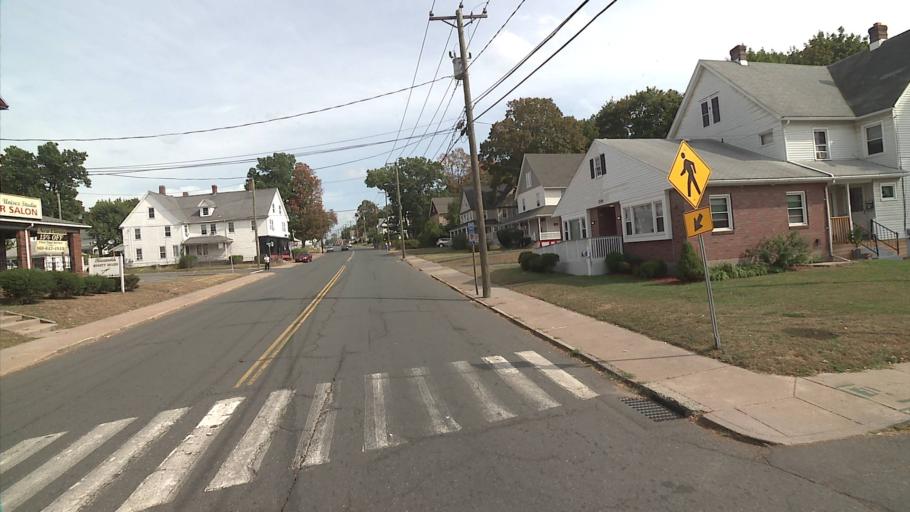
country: US
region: Connecticut
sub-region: Hartford County
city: Manchester
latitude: 41.7730
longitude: -72.5293
